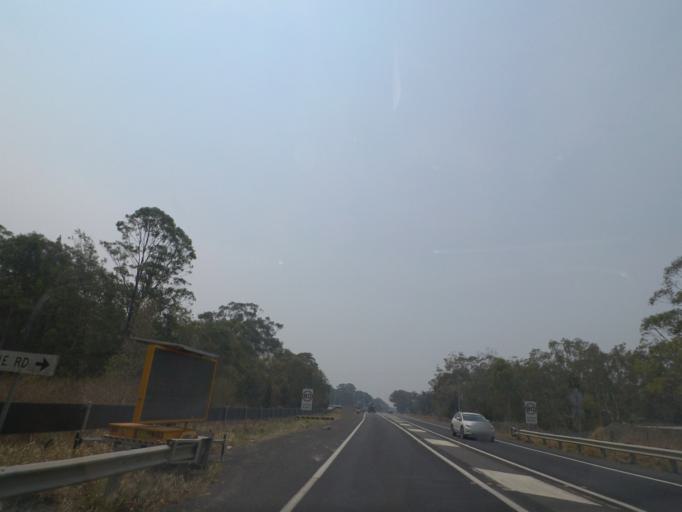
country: AU
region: New South Wales
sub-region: Ballina
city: Ballina
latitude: -28.9243
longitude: 153.4759
